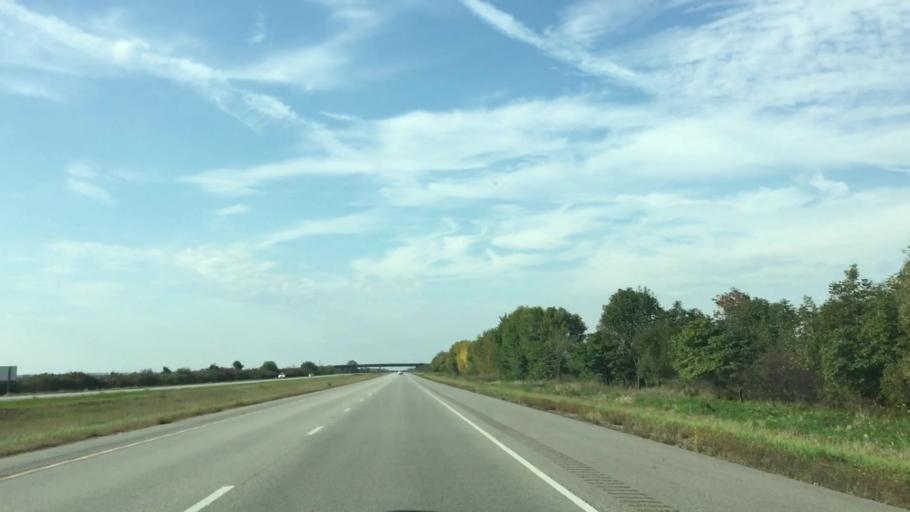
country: US
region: Illinois
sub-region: Rock Island County
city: Port Byron
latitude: 41.5887
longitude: -90.2004
